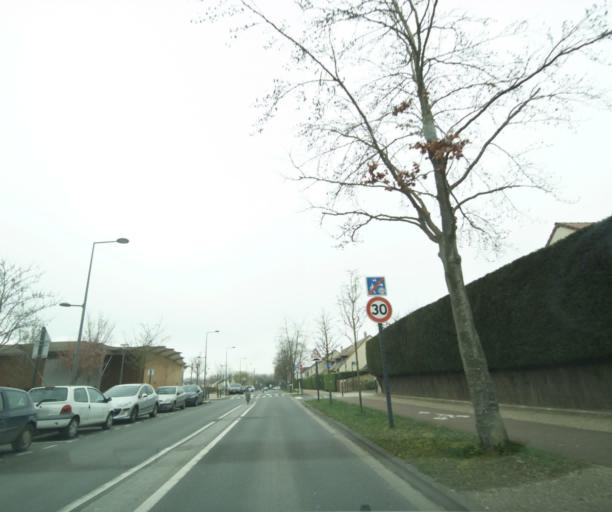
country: FR
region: Ile-de-France
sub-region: Departement du Val-d'Oise
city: Vaureal
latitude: 49.0475
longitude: 2.0180
